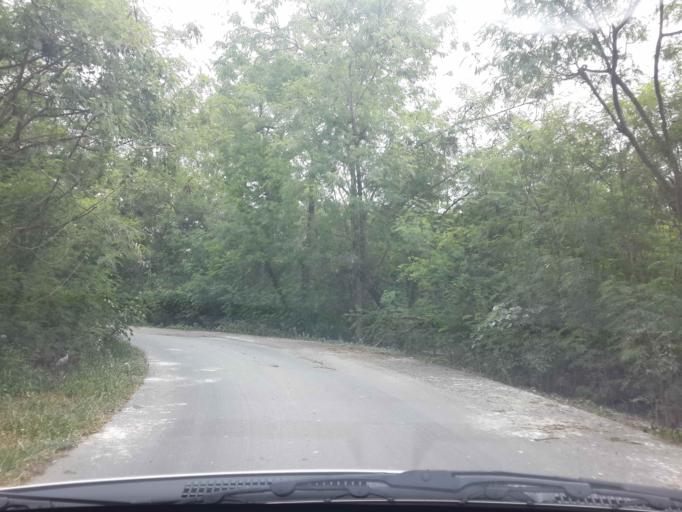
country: TH
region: Bangkok
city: Khan Na Yao
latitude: 13.8671
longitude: 100.7002
